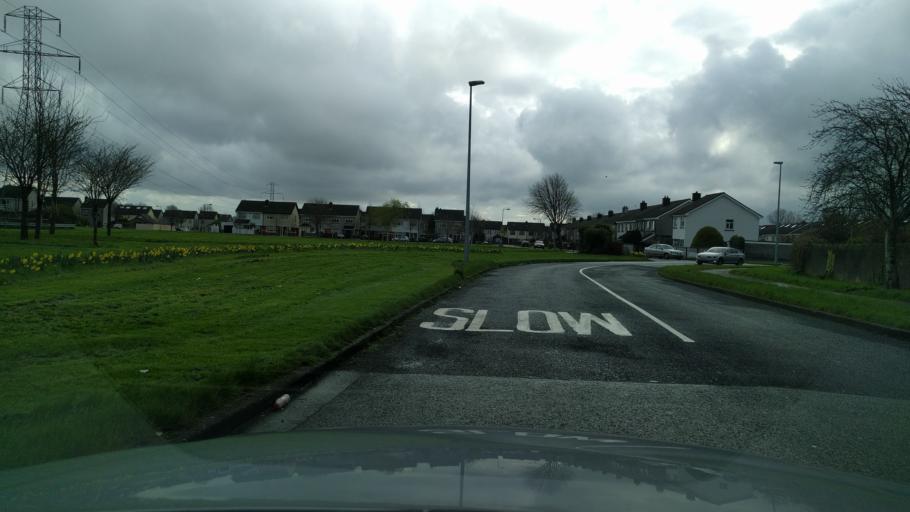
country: IE
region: Leinster
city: Tallaght
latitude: 53.2992
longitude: -6.3691
